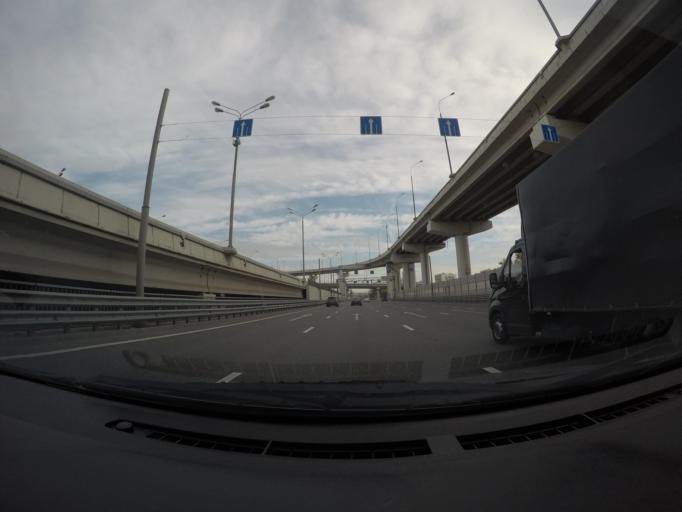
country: RU
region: Moscow
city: Novokhovrino
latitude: 55.8681
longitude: 37.5099
